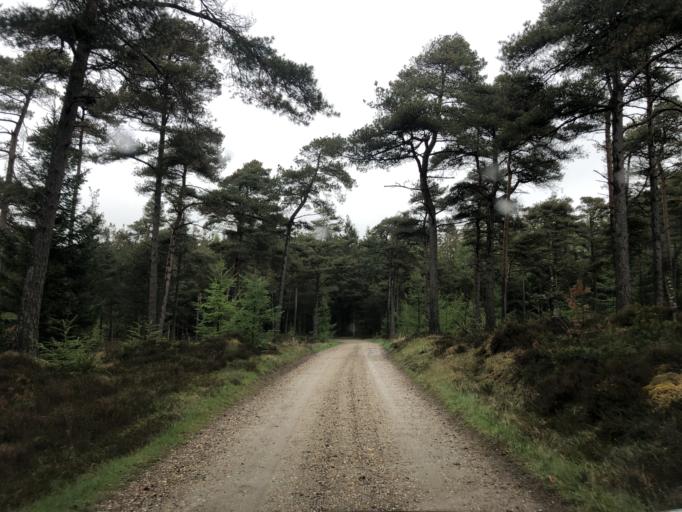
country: DK
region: Central Jutland
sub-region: Lemvig Kommune
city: Lemvig
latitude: 56.4545
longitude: 8.3954
